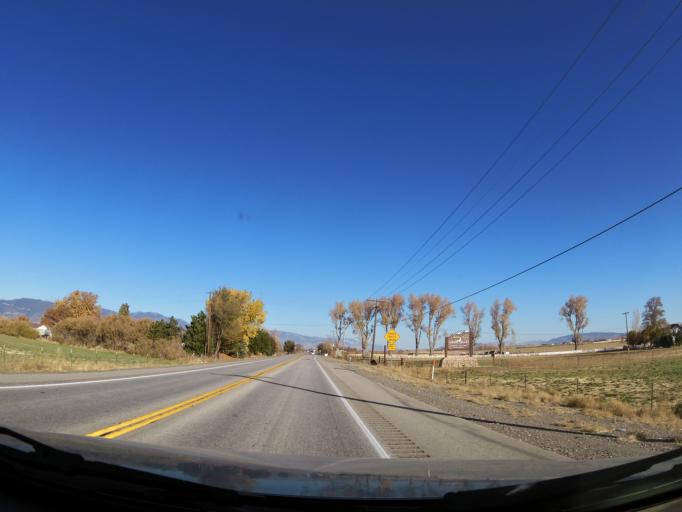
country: US
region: Nevada
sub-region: Douglas County
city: Gardnerville Ranchos
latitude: 38.8993
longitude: -119.7028
